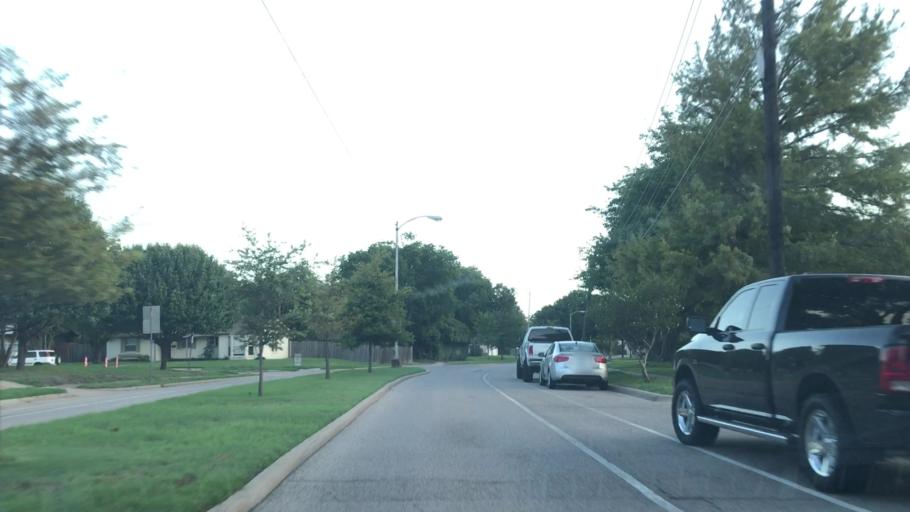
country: US
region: Texas
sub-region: Dallas County
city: Richardson
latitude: 32.9671
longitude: -96.7552
